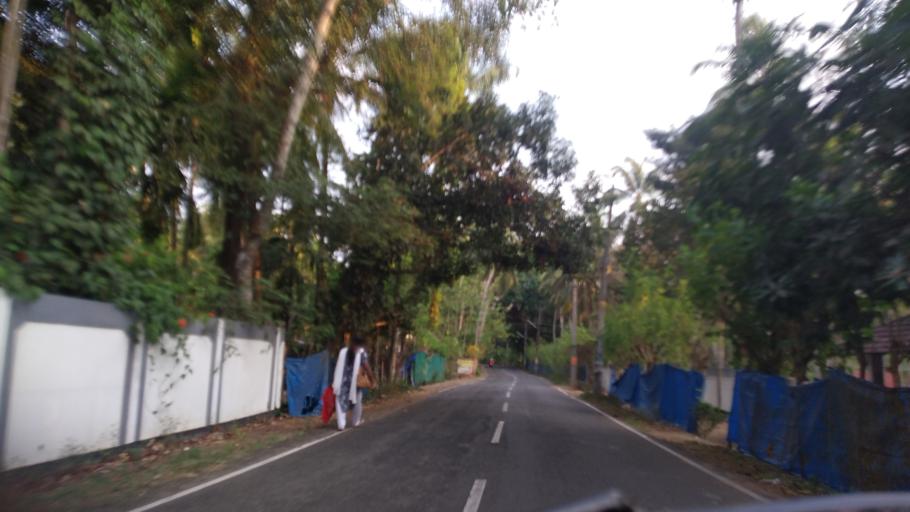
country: IN
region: Kerala
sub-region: Thrissur District
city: Thanniyam
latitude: 10.3787
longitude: 76.1018
